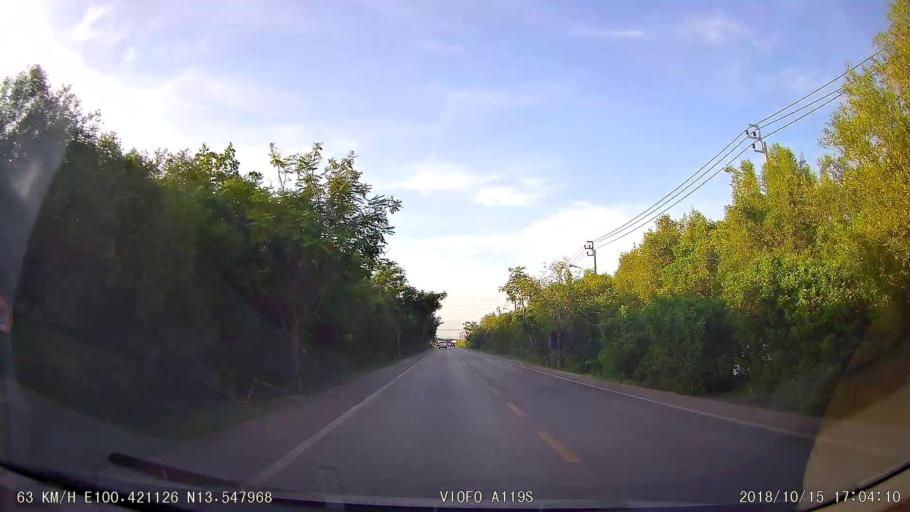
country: TH
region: Bangkok
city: Bang Khun Thian
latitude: 13.5481
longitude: 100.4211
